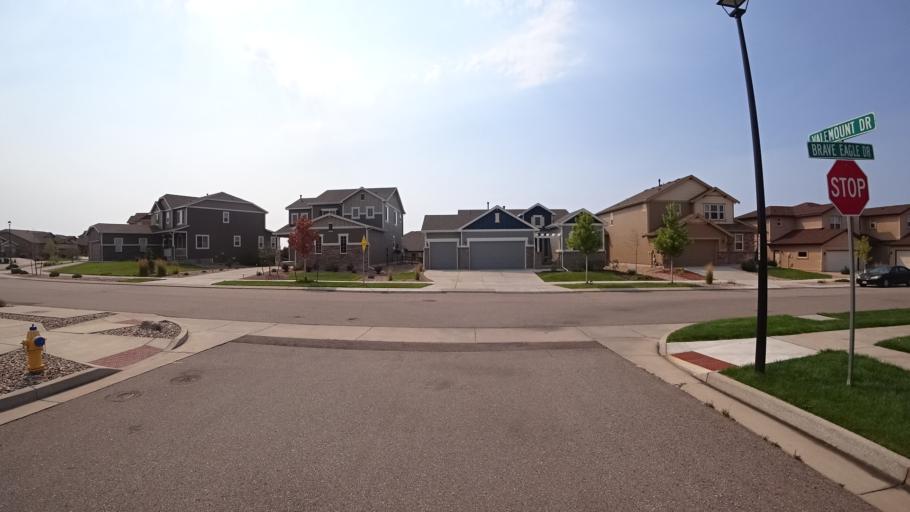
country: US
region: Colorado
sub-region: El Paso County
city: Black Forest
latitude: 38.9633
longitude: -104.7165
